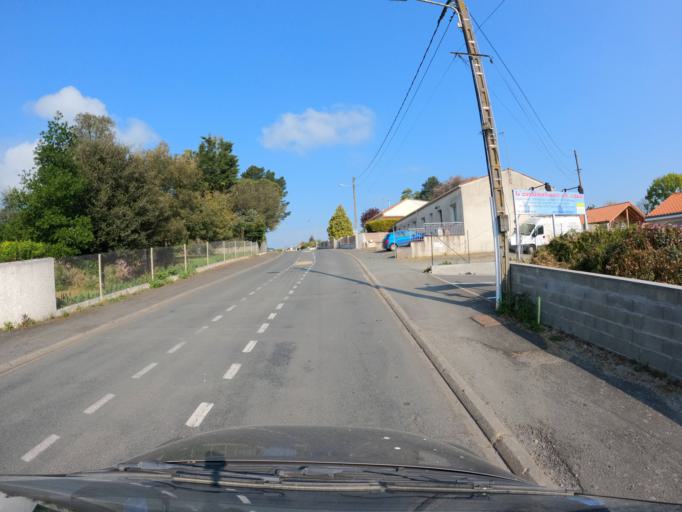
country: FR
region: Pays de la Loire
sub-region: Departement de Maine-et-Loire
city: La Romagne
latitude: 47.0626
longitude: -1.0261
